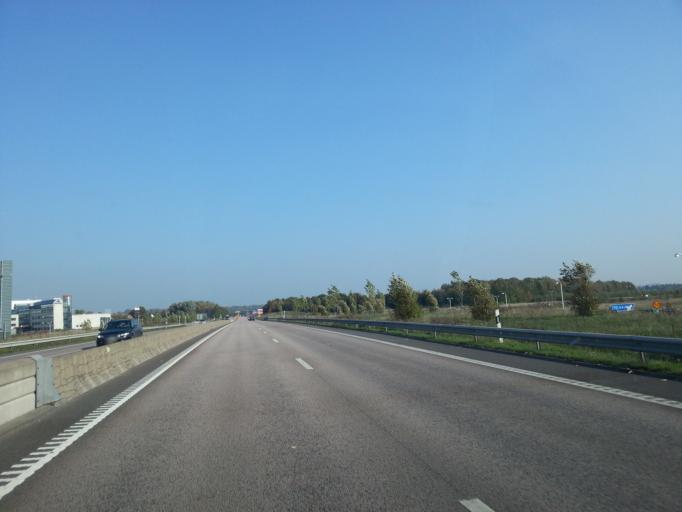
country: SE
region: Skane
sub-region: Lunds Kommun
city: Lund
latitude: 55.6858
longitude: 13.1966
